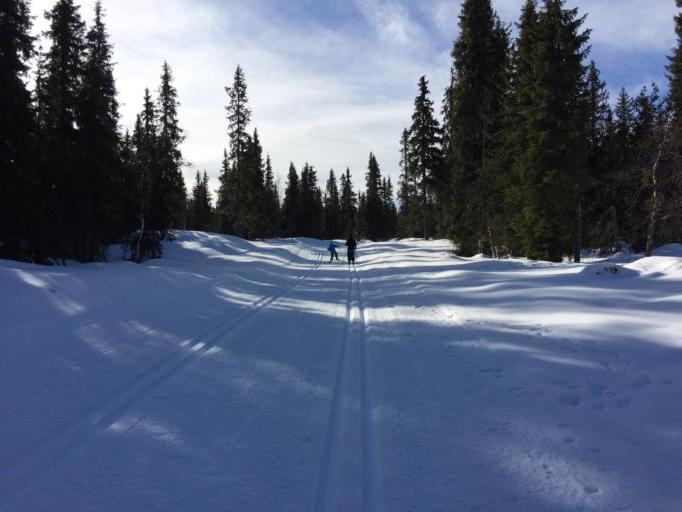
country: NO
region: Oppland
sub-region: Gausdal
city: Segalstad bru
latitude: 61.3269
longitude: 10.0789
